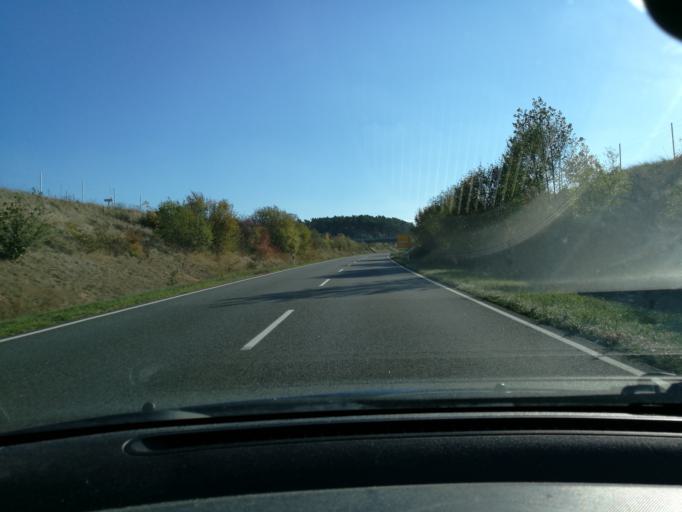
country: DE
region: Lower Saxony
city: Dahlem
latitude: 53.1900
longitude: 10.7579
